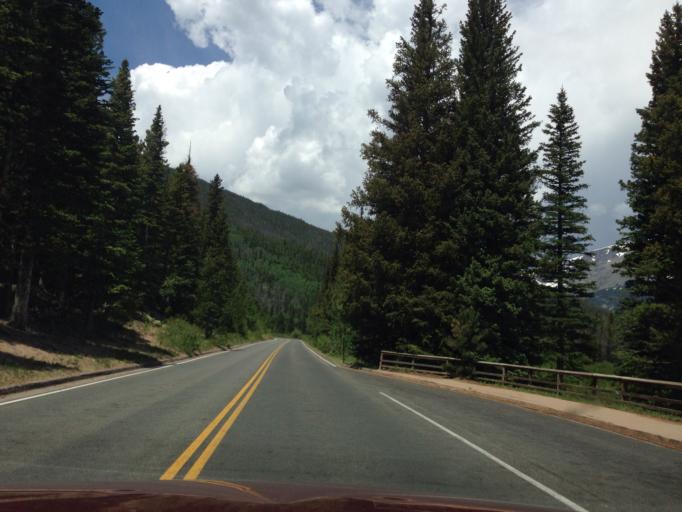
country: US
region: Colorado
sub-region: Larimer County
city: Estes Park
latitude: 40.3990
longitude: -105.6412
